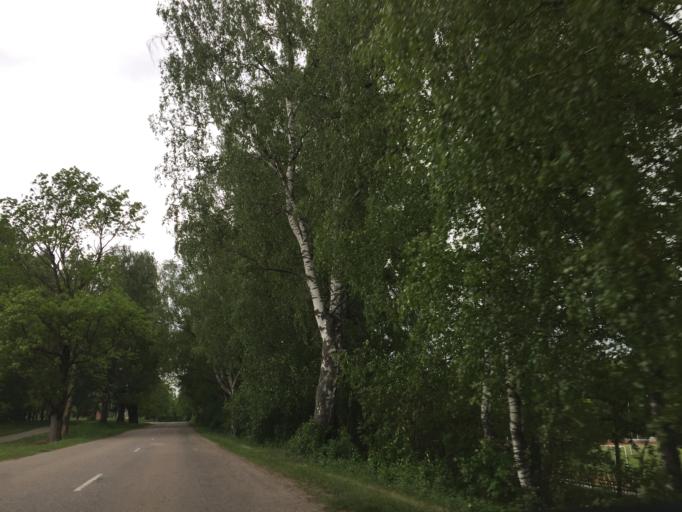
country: LV
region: Preilu Rajons
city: Preili
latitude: 56.0613
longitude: 26.7713
